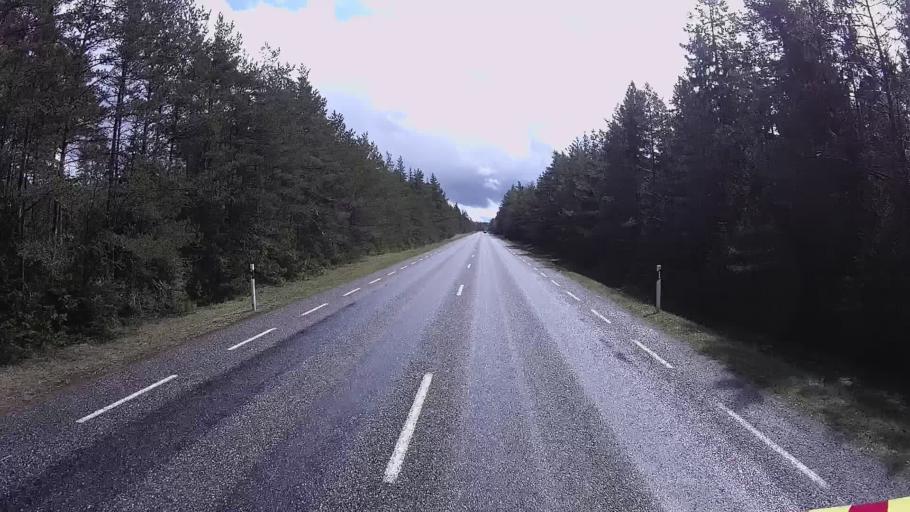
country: EE
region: Hiiumaa
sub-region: Kaerdla linn
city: Kardla
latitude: 58.9860
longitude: 22.7973
